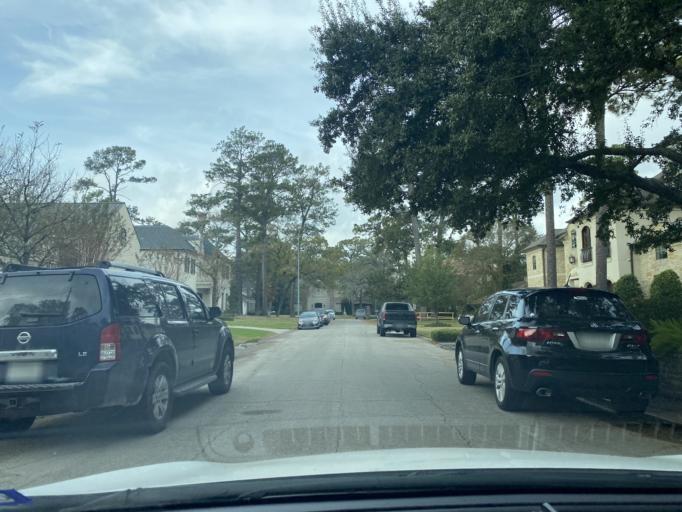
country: US
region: Texas
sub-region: Harris County
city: Hunters Creek Village
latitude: 29.7674
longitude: -95.4697
